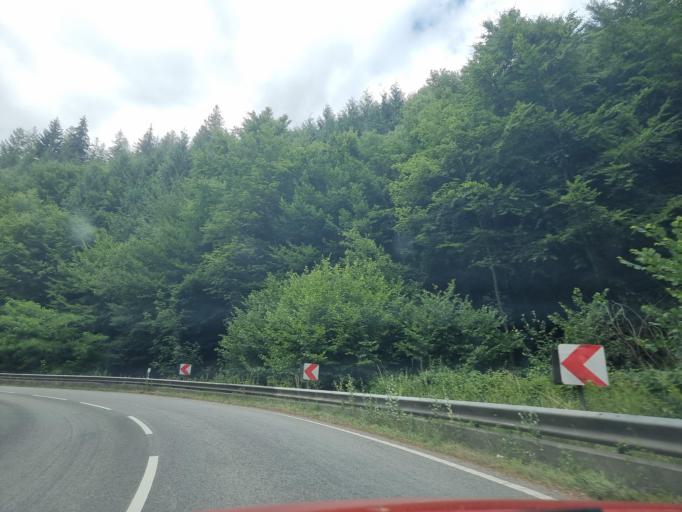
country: DE
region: Rheinland-Pfalz
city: Kenn
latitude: 49.8449
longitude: 6.7057
